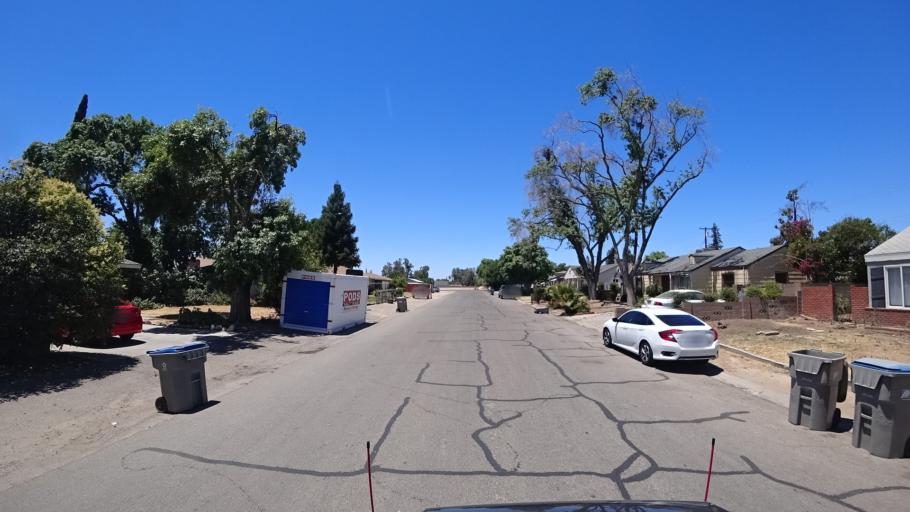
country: US
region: California
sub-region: Fresno County
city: Fresno
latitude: 36.7903
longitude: -119.8115
